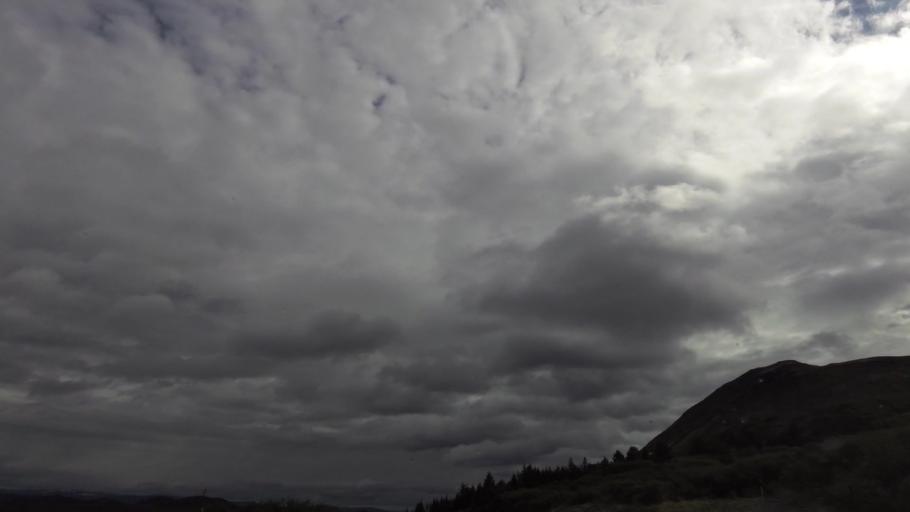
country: IS
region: West
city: Stykkisholmur
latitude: 65.5197
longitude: -22.1160
